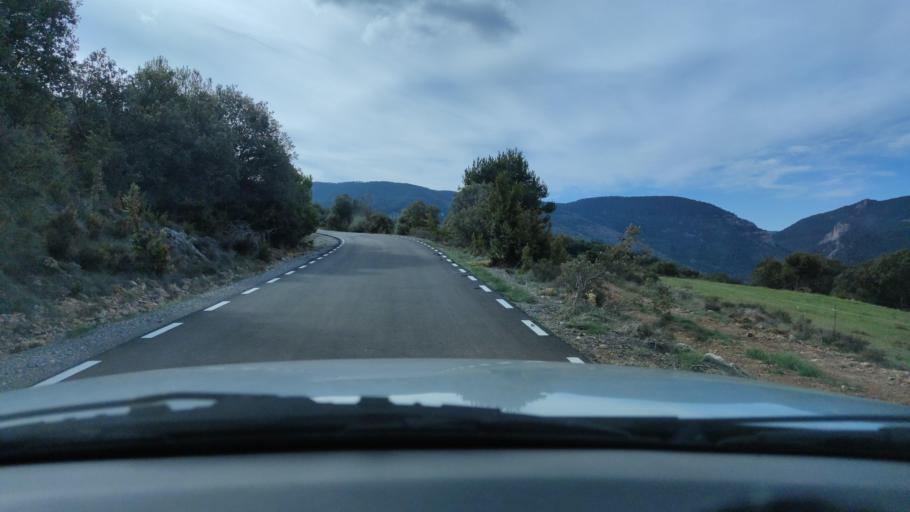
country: ES
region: Catalonia
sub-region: Provincia de Lleida
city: Coll de Nargo
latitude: 42.2383
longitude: 1.4040
